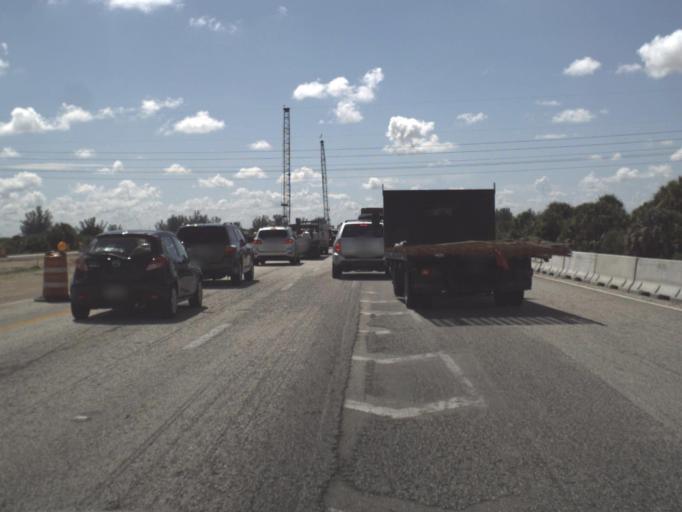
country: US
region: Florida
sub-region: Lee County
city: Tice
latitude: 26.7111
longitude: -81.8089
